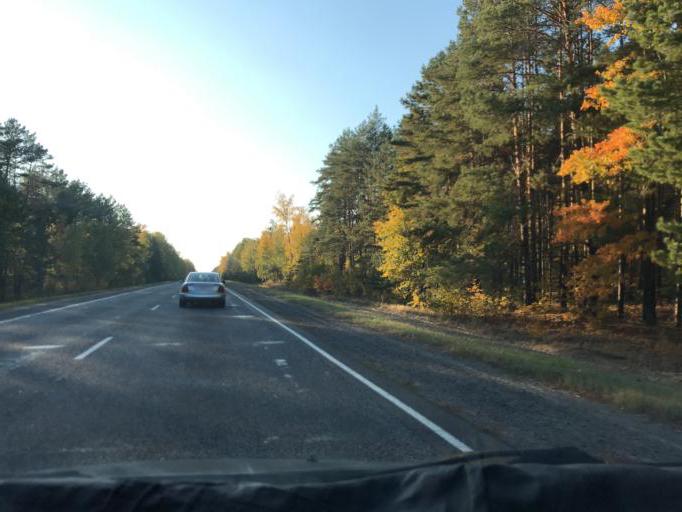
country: BY
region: Gomel
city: Zhytkavichy
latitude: 52.2726
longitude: 28.0719
